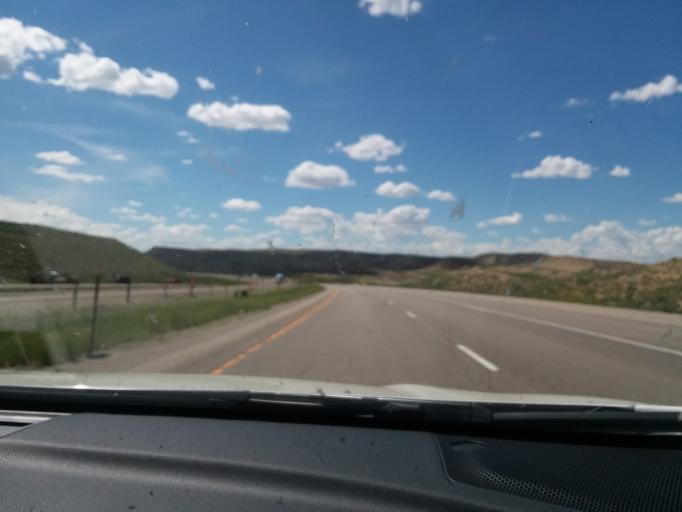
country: US
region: Wyoming
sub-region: Sweetwater County
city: Rock Springs
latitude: 41.6719
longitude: -108.7363
